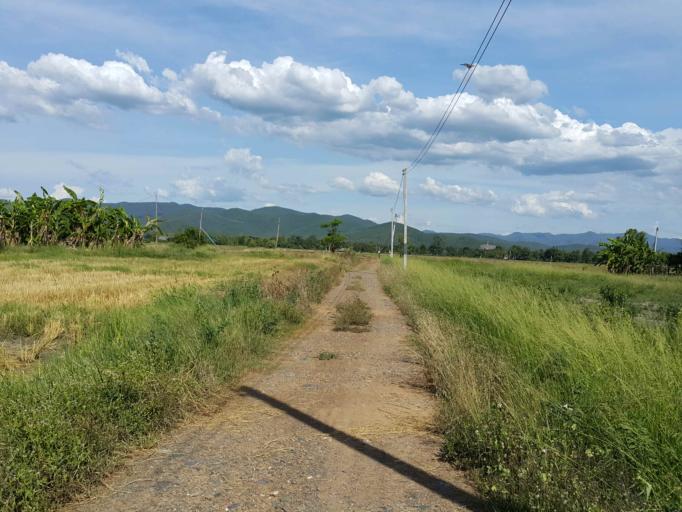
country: TH
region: Chiang Mai
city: San Kamphaeng
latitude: 18.7992
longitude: 99.1535
